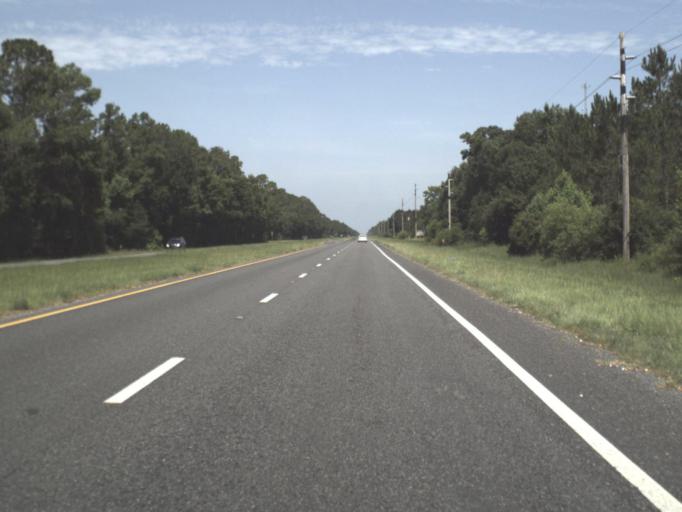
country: US
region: Florida
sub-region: Dixie County
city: Cross City
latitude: 29.6503
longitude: -83.1644
